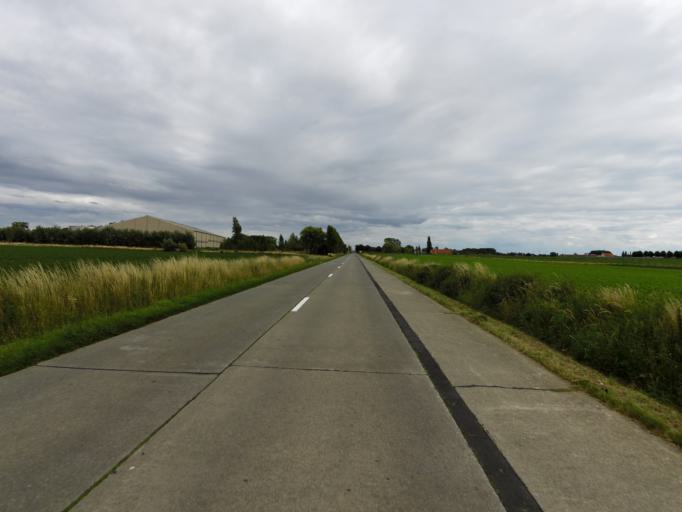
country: BE
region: Flanders
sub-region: Provincie West-Vlaanderen
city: Koekelare
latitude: 51.0645
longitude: 3.0007
